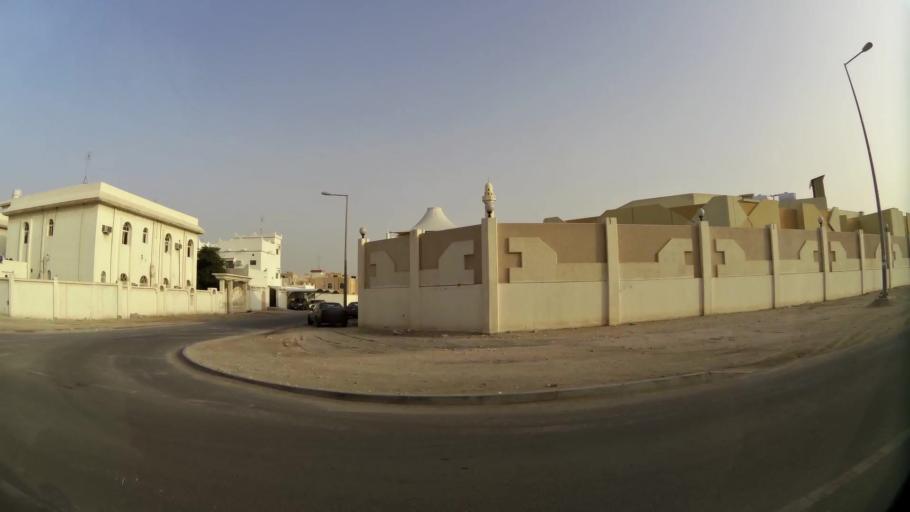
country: QA
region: Baladiyat ar Rayyan
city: Ar Rayyan
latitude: 25.2431
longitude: 51.4488
